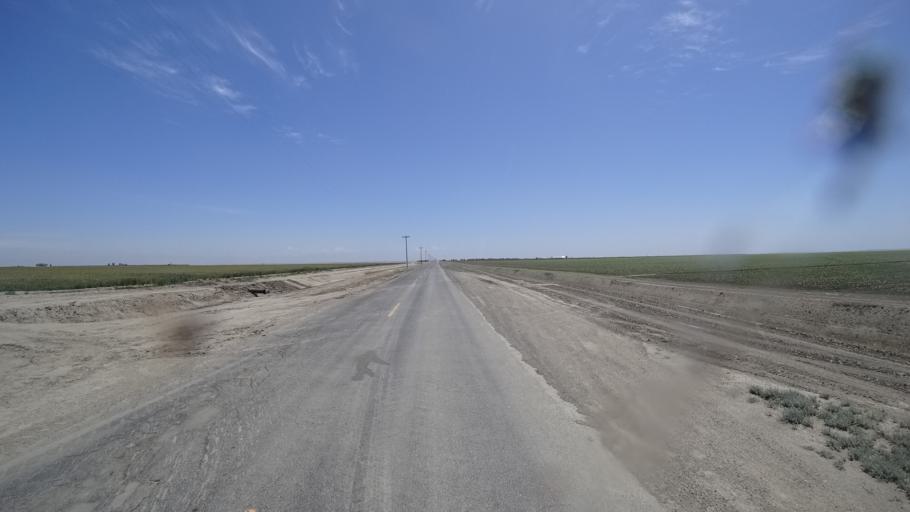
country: US
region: California
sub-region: Kings County
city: Corcoran
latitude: 36.1161
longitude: -119.6712
